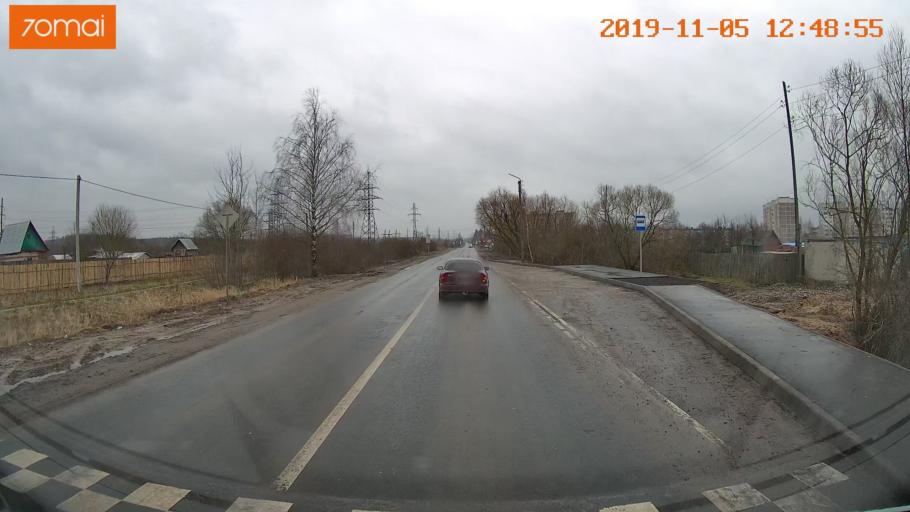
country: RU
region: Ivanovo
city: Kokhma
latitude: 56.9578
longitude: 41.1014
